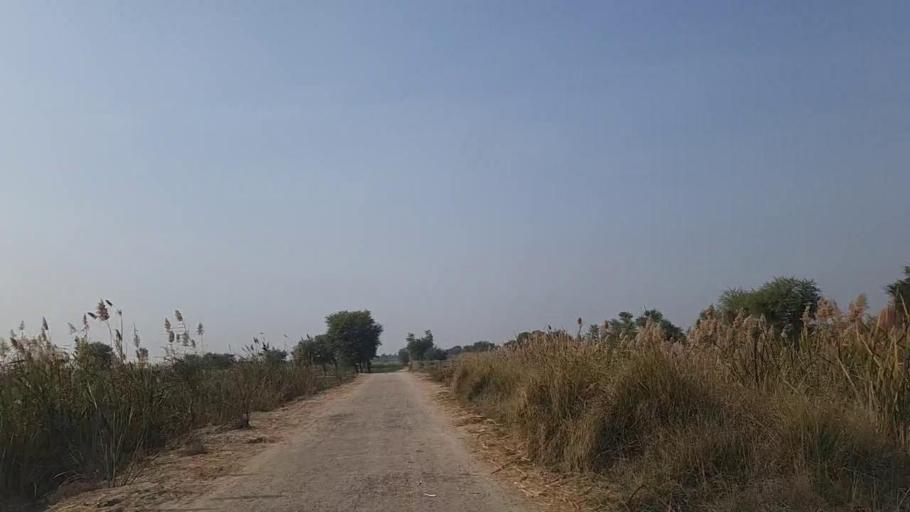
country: PK
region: Sindh
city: Daur
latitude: 26.5063
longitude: 68.4371
